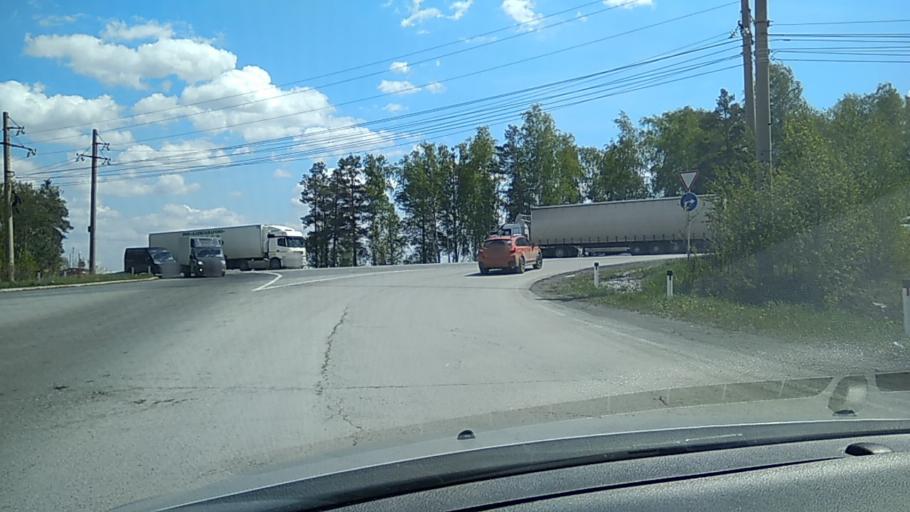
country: RU
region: Sverdlovsk
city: Istok
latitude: 56.7548
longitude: 60.7583
